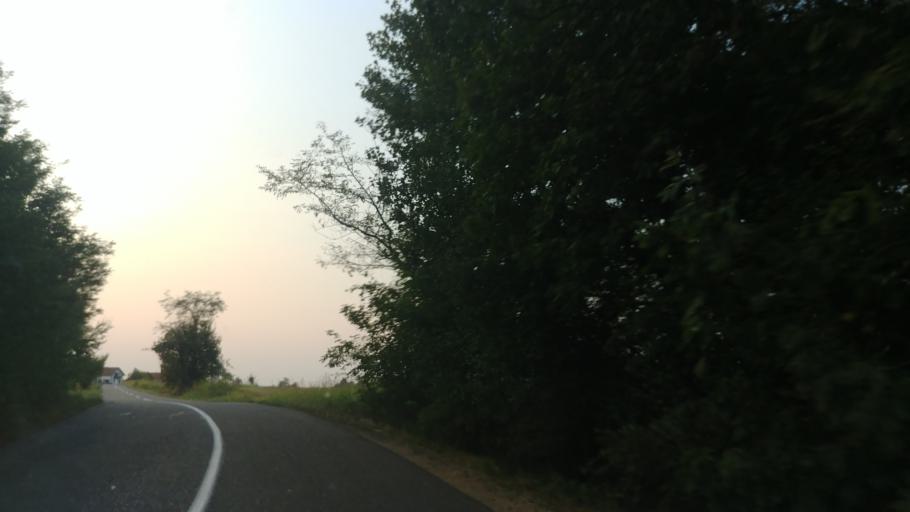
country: BA
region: Republika Srpska
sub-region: Opstina Ugljevik
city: Ugljevik
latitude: 44.7349
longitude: 18.9972
